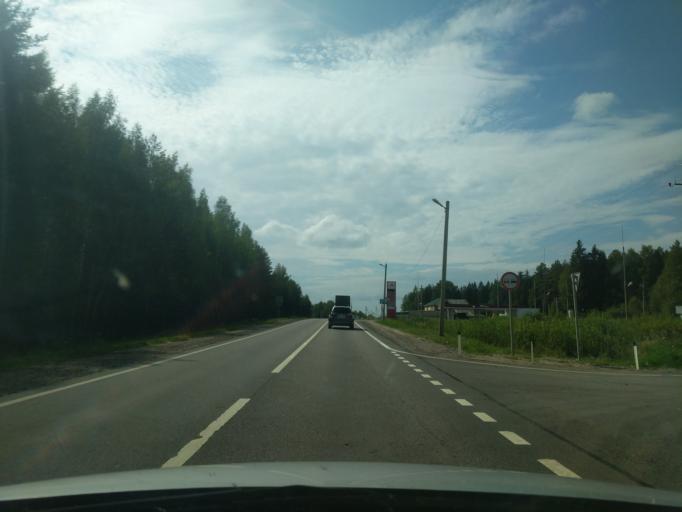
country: RU
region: Kostroma
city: Kadyy
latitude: 57.8009
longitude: 43.2070
